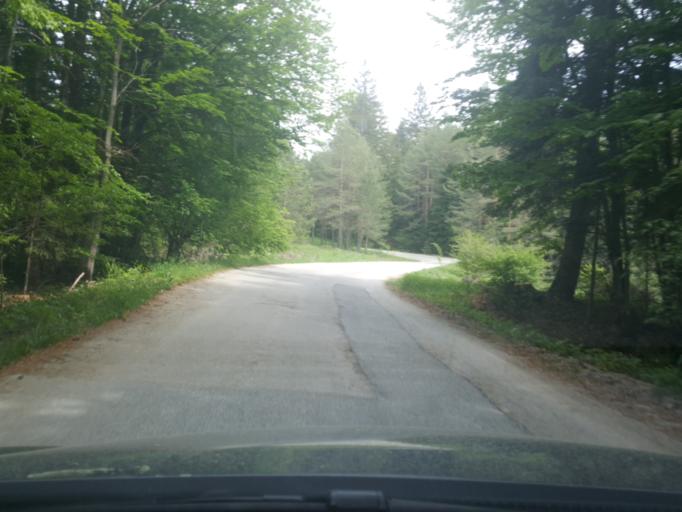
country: RS
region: Central Serbia
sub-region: Zlatiborski Okrug
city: Bajina Basta
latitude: 43.8906
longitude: 19.5299
